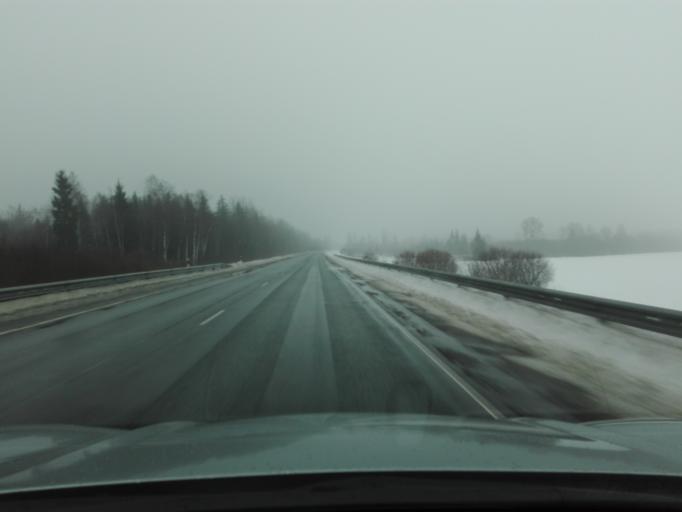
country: EE
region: Raplamaa
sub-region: Kohila vald
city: Kohila
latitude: 59.1980
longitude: 24.7846
